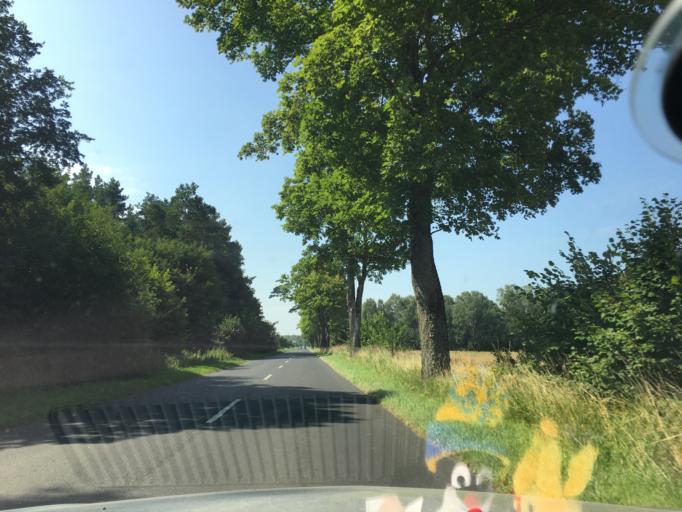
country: PL
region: West Pomeranian Voivodeship
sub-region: Powiat kamienski
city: Dziwnow
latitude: 54.0106
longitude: 14.8484
